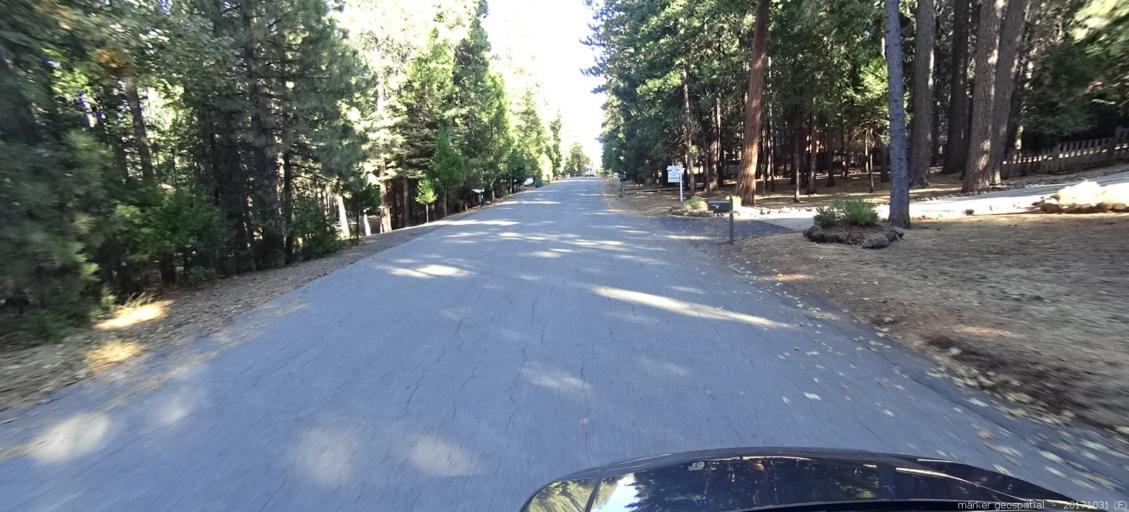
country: US
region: California
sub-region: Shasta County
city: Shingletown
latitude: 40.5045
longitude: -121.9082
